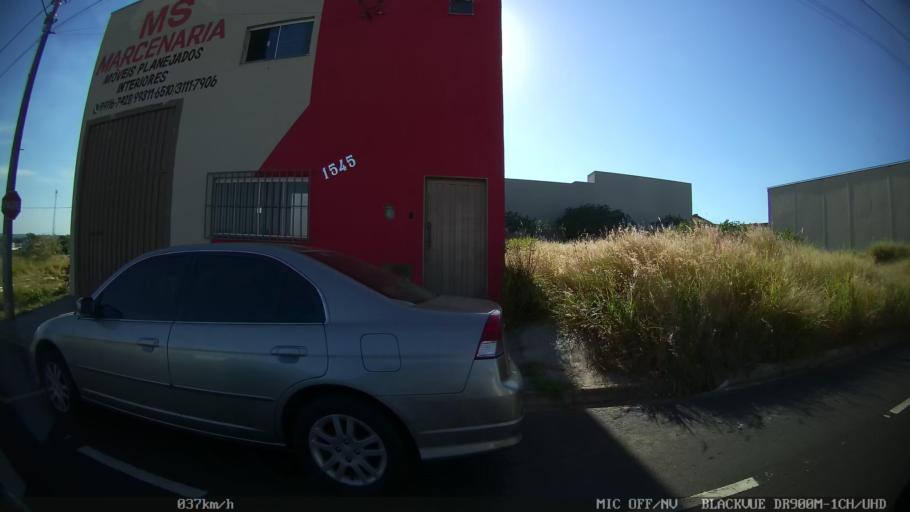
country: BR
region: Sao Paulo
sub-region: Franca
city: Franca
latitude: -20.5140
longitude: -47.4271
